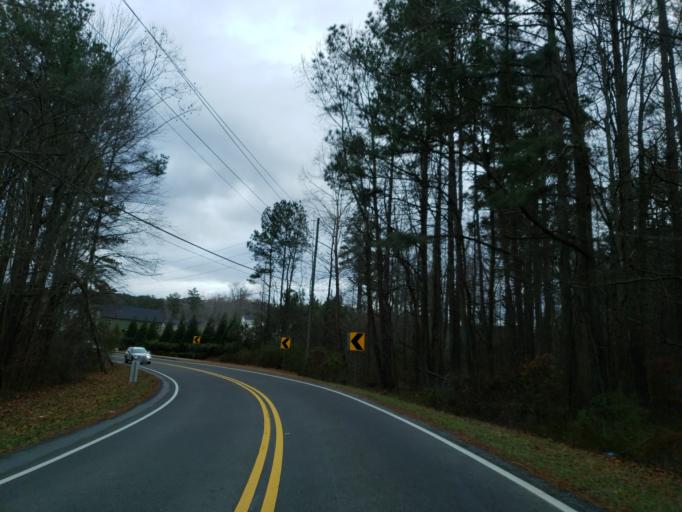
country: US
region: Georgia
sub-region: Cobb County
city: Fair Oaks
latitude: 33.9197
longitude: -84.6012
